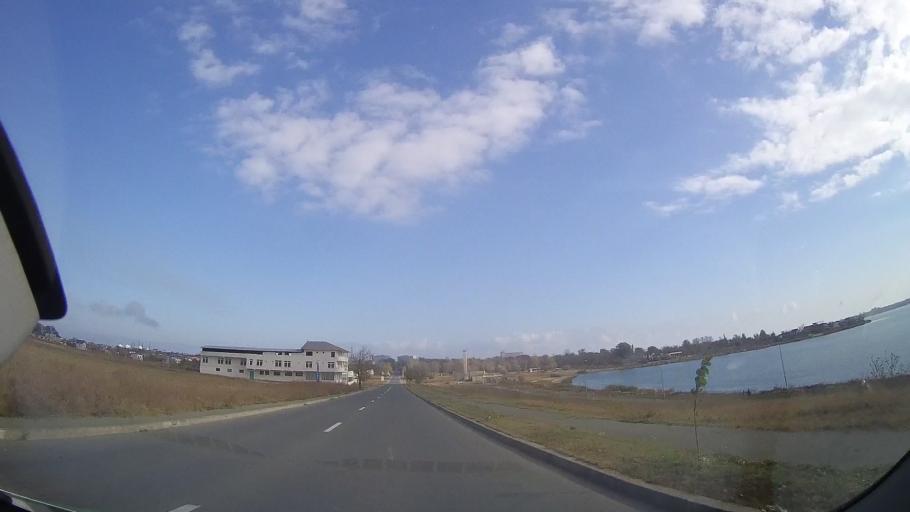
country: RO
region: Constanta
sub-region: Oras Eforie
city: Eforie Nord
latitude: 44.0580
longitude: 28.6162
